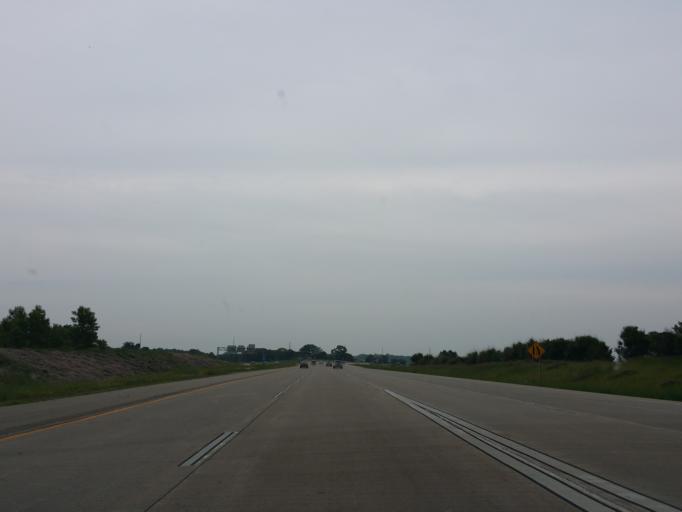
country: US
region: Wisconsin
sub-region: Dane County
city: Monona
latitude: 43.1027
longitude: -89.2758
